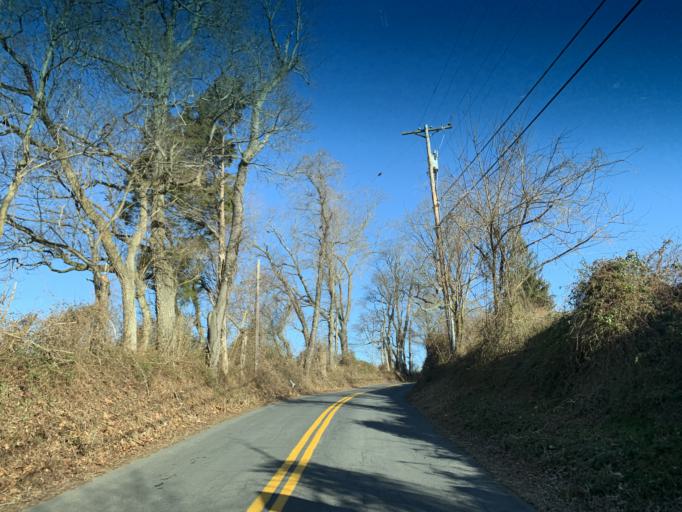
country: US
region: Maryland
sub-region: Harford County
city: Aberdeen
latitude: 39.5983
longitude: -76.2253
